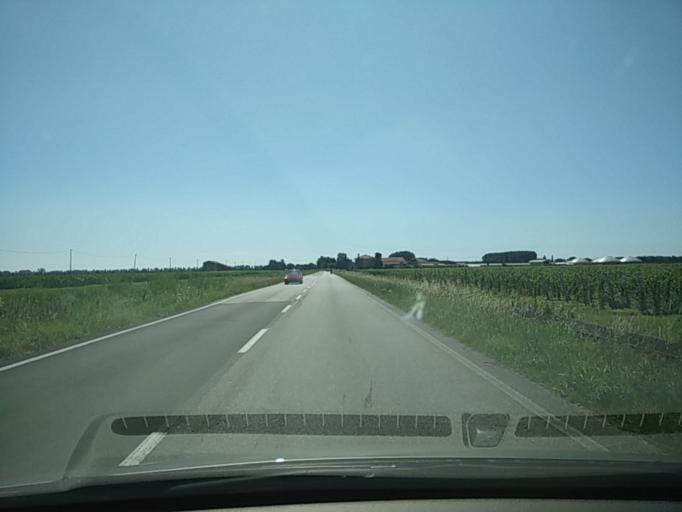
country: IT
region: Veneto
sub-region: Provincia di Venezia
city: San Giorgio di Livenza
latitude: 45.6331
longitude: 12.7715
